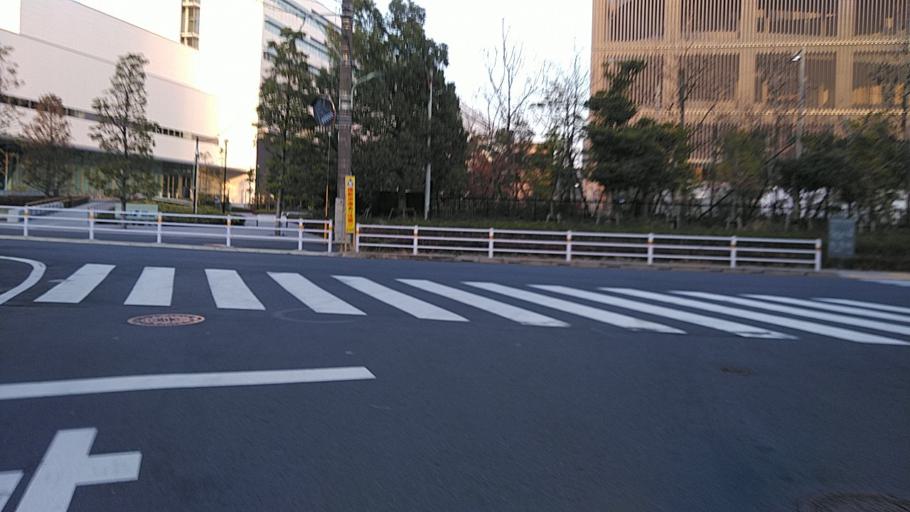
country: JP
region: Kanagawa
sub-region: Kawasaki-shi
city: Kawasaki
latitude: 35.5536
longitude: 139.7481
